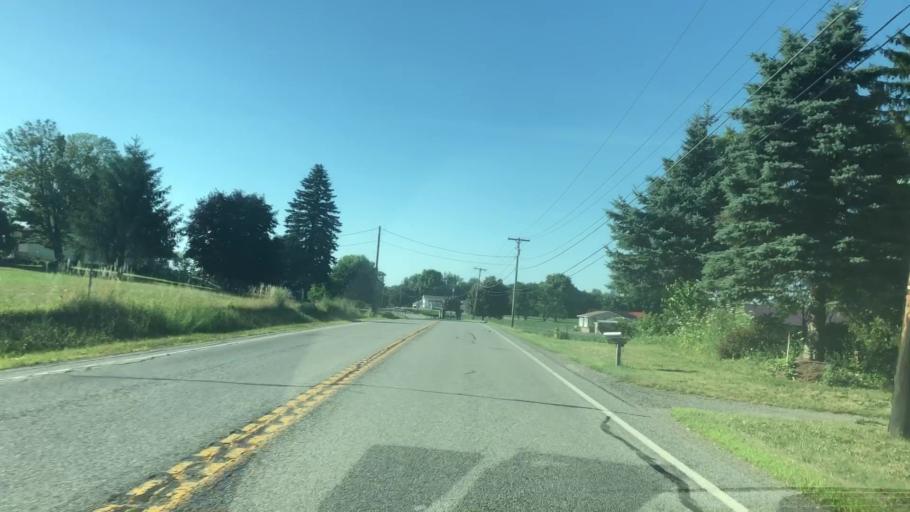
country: US
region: New York
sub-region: Wayne County
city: Ontario
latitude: 43.1891
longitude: -77.2916
